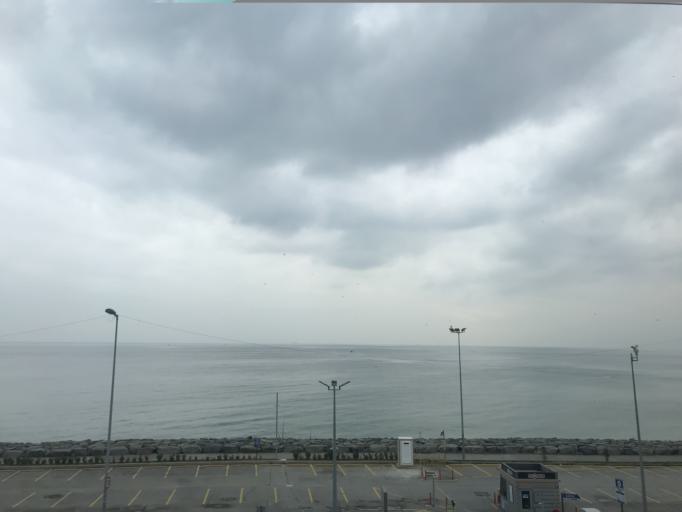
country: TR
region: Istanbul
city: Bahcelievler
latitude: 40.9765
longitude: 28.7766
